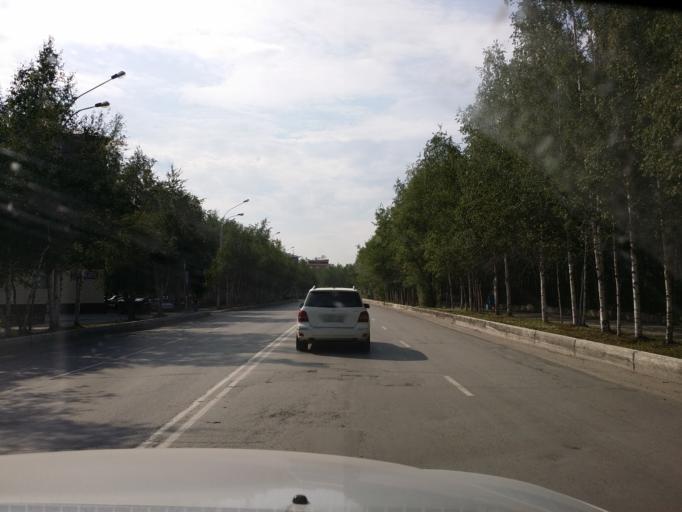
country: RU
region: Khanty-Mansiyskiy Avtonomnyy Okrug
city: Nizhnevartovsk
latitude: 60.9368
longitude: 76.5705
